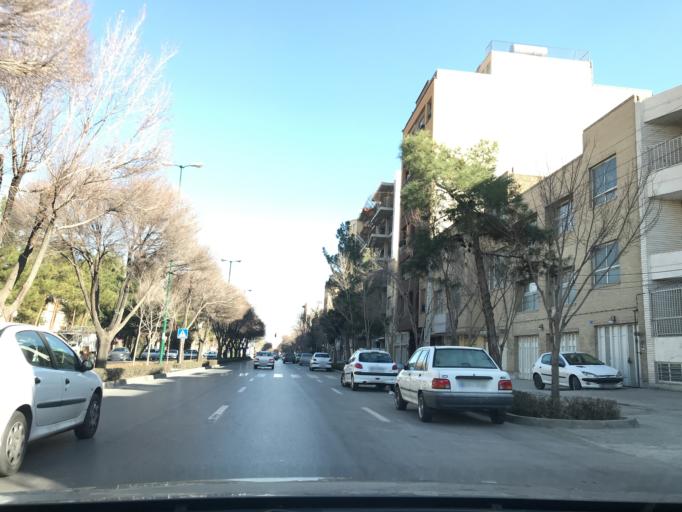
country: IR
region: Isfahan
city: Isfahan
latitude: 32.6149
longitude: 51.6679
